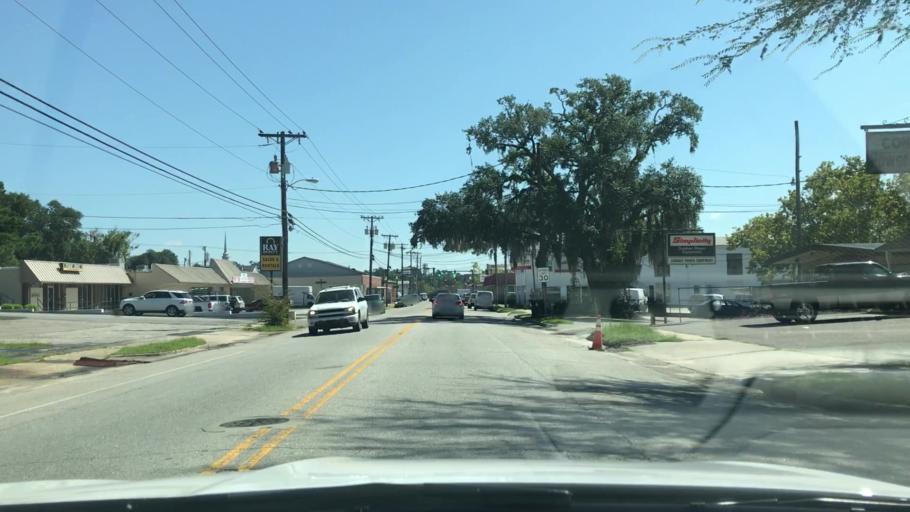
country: US
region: South Carolina
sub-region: Horry County
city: Conway
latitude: 33.8341
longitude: -79.0516
